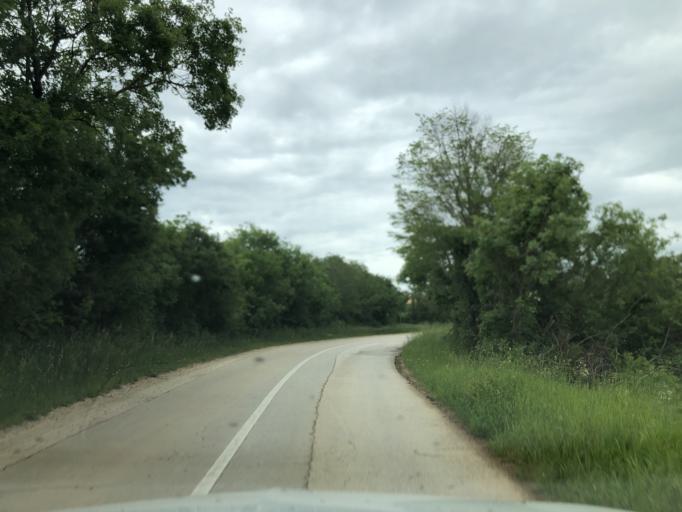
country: HR
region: Istarska
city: Buje
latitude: 45.4475
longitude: 13.6419
